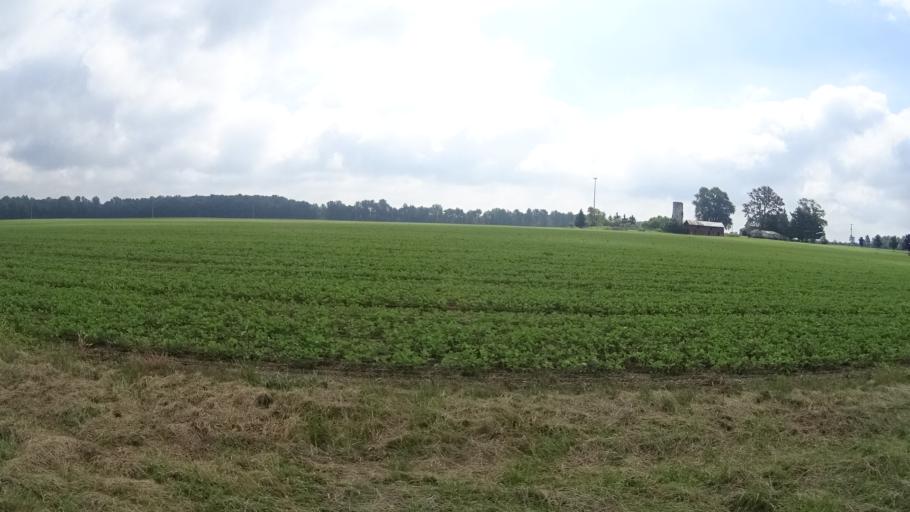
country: US
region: Ohio
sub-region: Huron County
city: Wakeman
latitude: 41.2858
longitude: -82.4655
